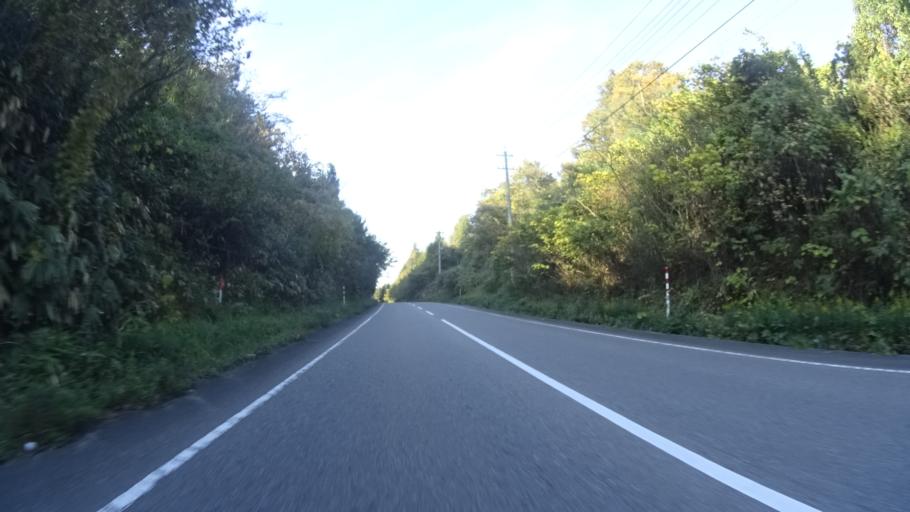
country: JP
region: Ishikawa
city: Hakui
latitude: 37.0096
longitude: 136.7993
